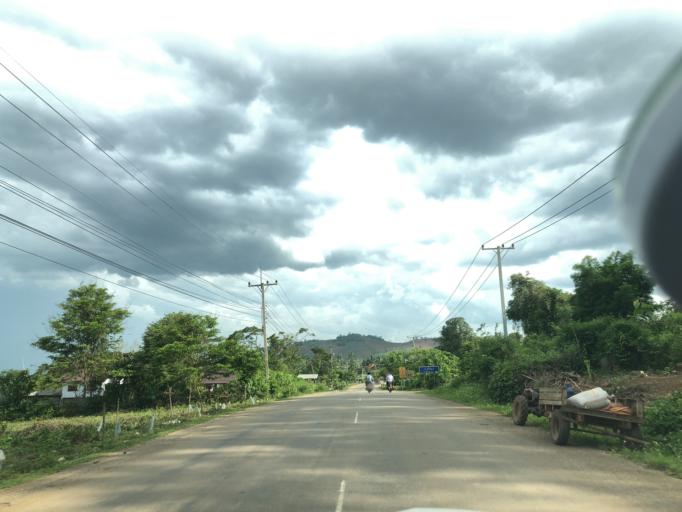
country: TH
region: Uttaradit
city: Ban Khok
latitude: 18.1431
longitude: 101.3819
